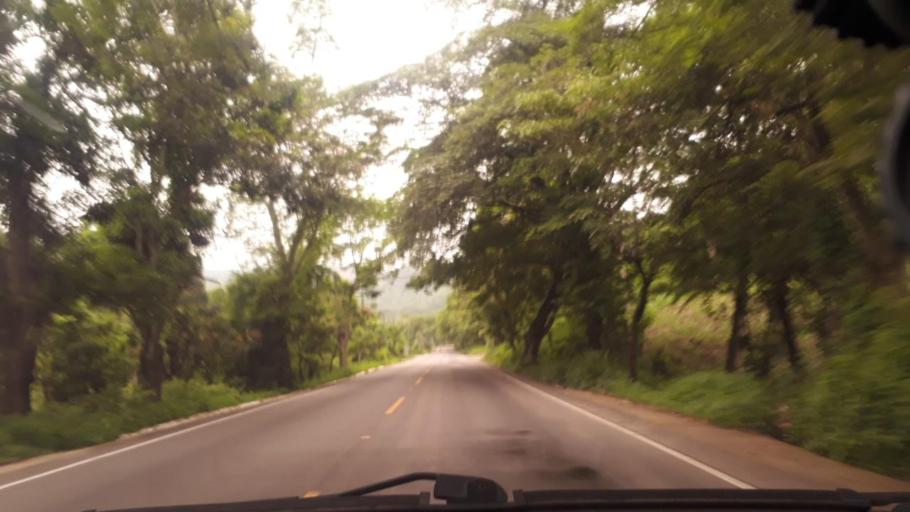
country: GT
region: Chiquimula
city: Quezaltepeque
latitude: 14.6274
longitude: -89.4514
